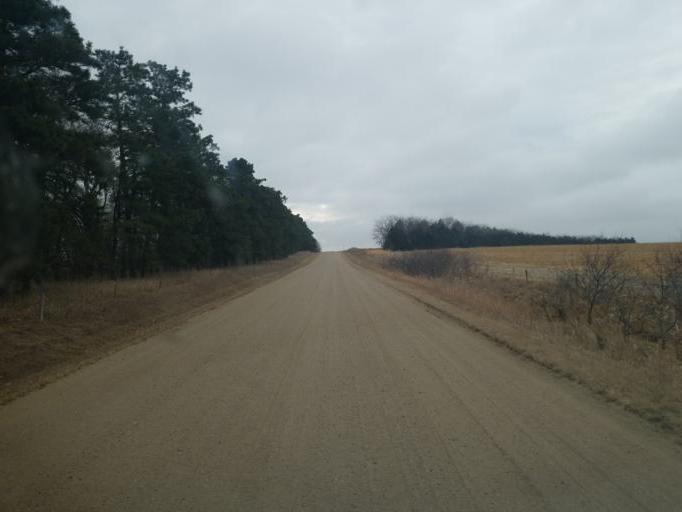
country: US
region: Nebraska
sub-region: Pierce County
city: Plainview
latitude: 42.4273
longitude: -97.7960
